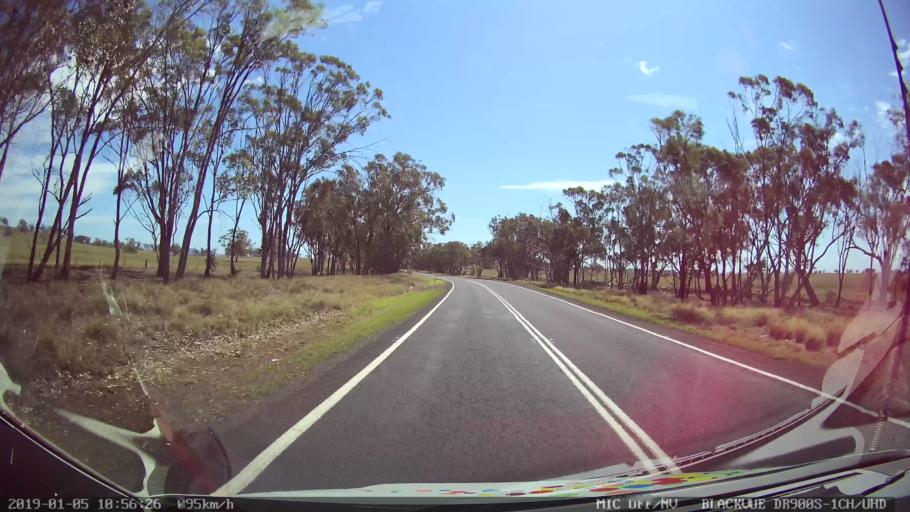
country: AU
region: New South Wales
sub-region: Warrumbungle Shire
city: Coonabarabran
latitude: -31.4414
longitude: 149.1580
